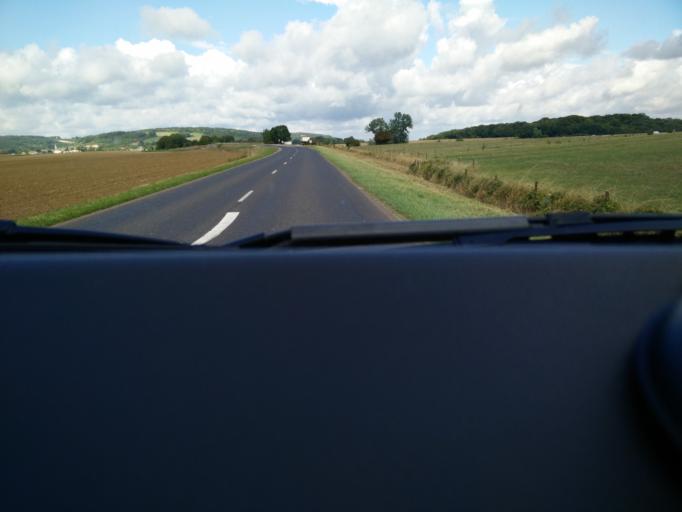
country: FR
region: Lorraine
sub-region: Departement de la Meuse
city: Etain
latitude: 49.1133
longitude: 5.5880
